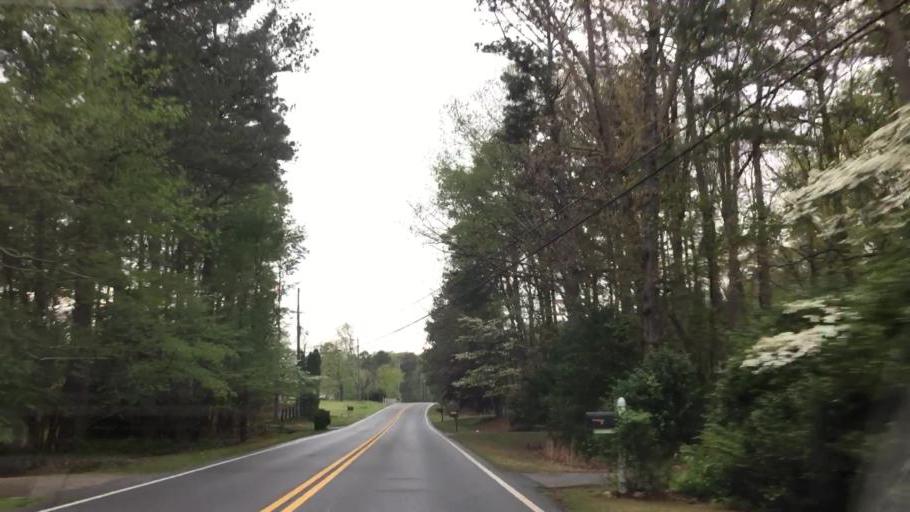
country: US
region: Georgia
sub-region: Fulton County
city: Milton
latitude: 34.1740
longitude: -84.2972
